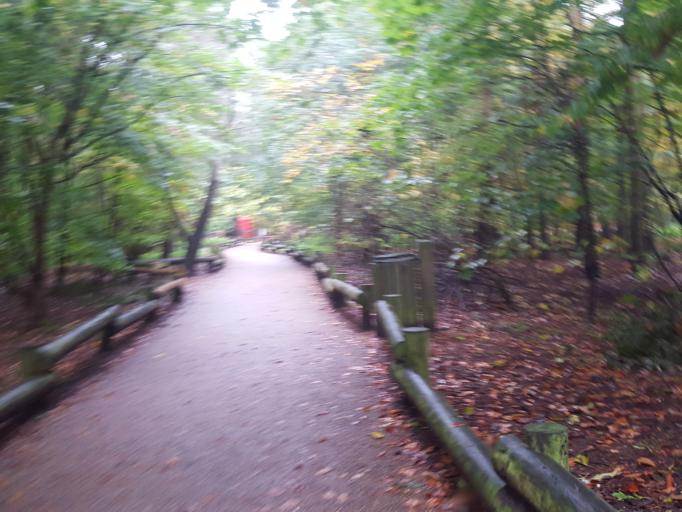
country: GB
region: England
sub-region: Norfolk
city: Weeting
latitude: 52.3911
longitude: 0.6397
